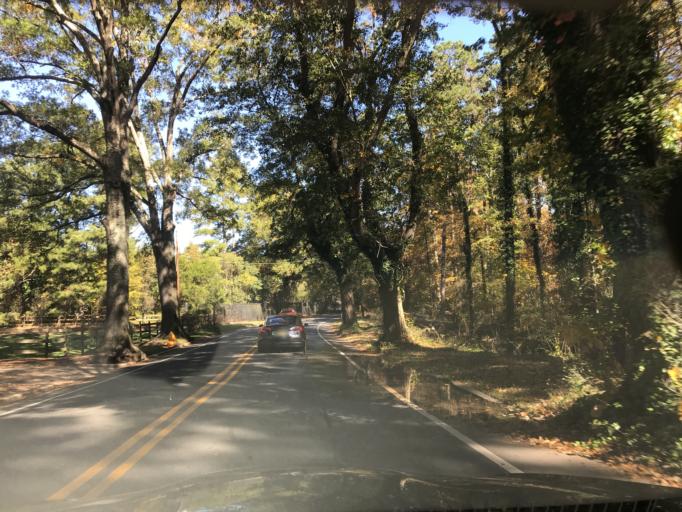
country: US
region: North Carolina
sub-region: Durham County
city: Durham
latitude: 35.9925
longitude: -78.9399
